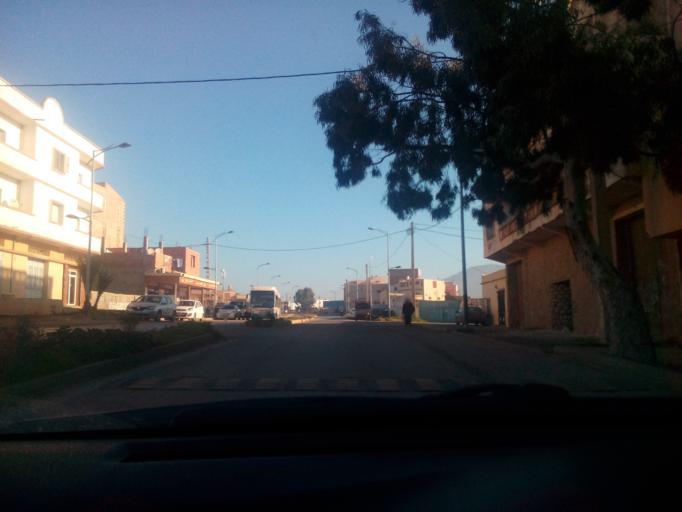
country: DZ
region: Oran
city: Bir el Djir
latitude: 35.7583
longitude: -0.5366
